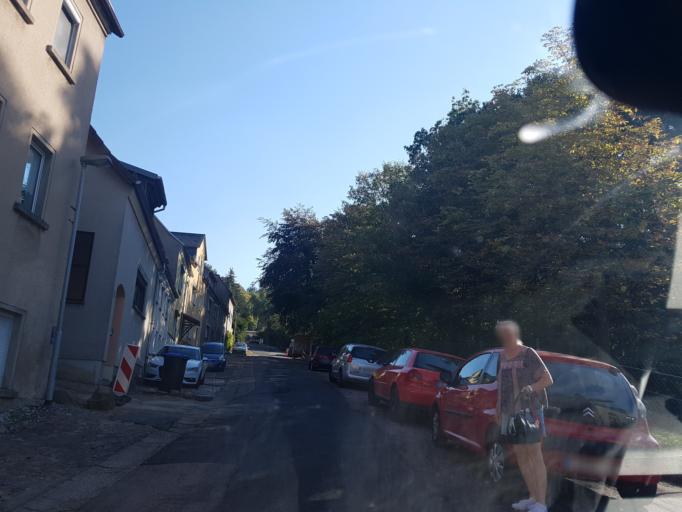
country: DE
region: Saxony
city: Waldheim
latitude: 51.0692
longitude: 13.0249
